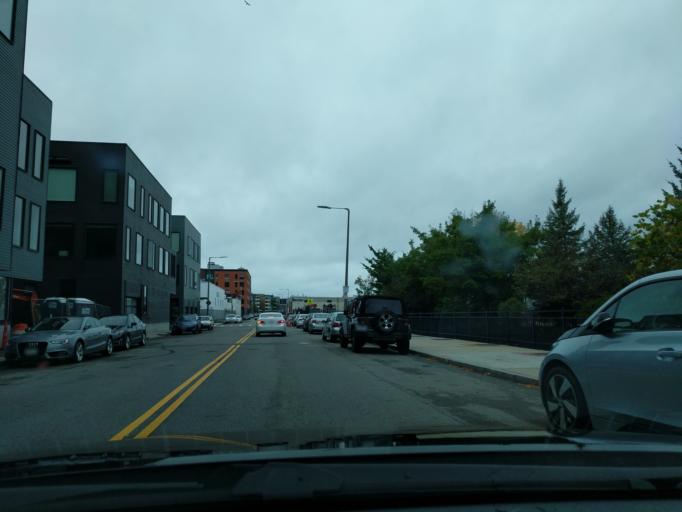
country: US
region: Massachusetts
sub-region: Suffolk County
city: South Boston
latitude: 42.3381
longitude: -71.0391
